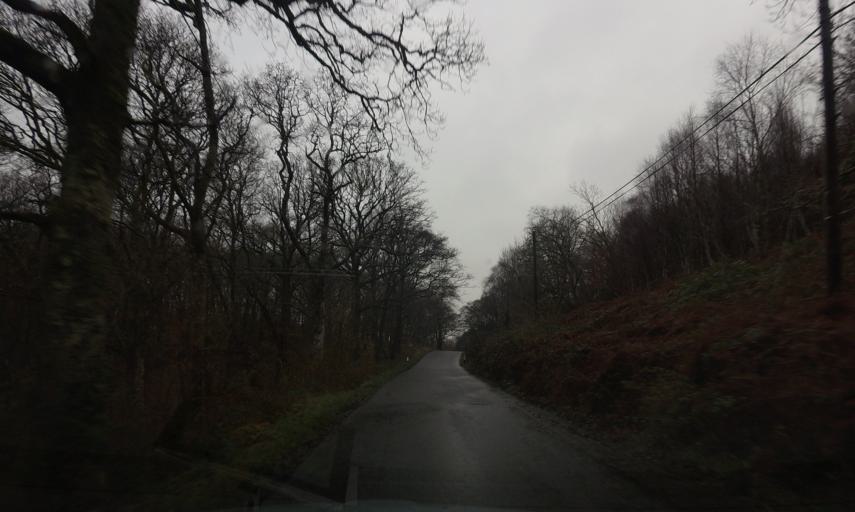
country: GB
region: Scotland
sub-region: West Dunbartonshire
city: Balloch
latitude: 56.1218
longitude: -4.5948
